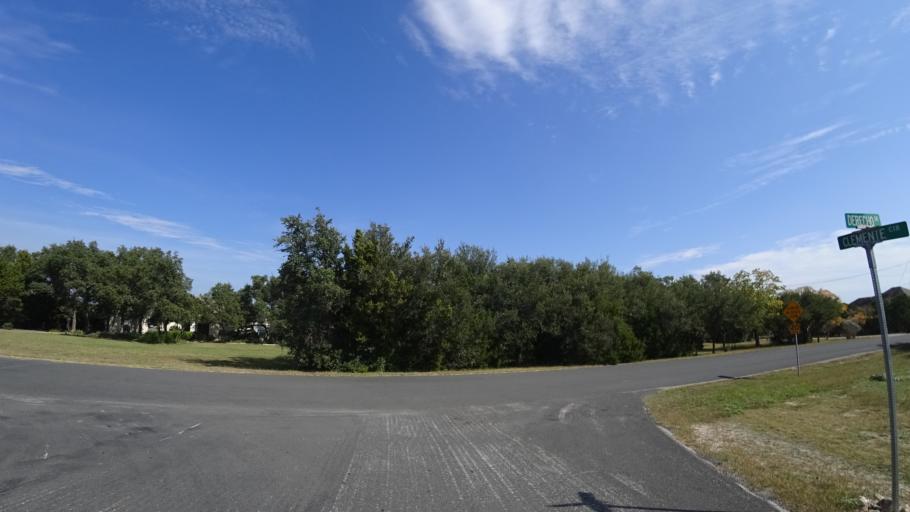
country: US
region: Texas
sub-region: Travis County
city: Bee Cave
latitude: 30.2250
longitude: -97.9363
